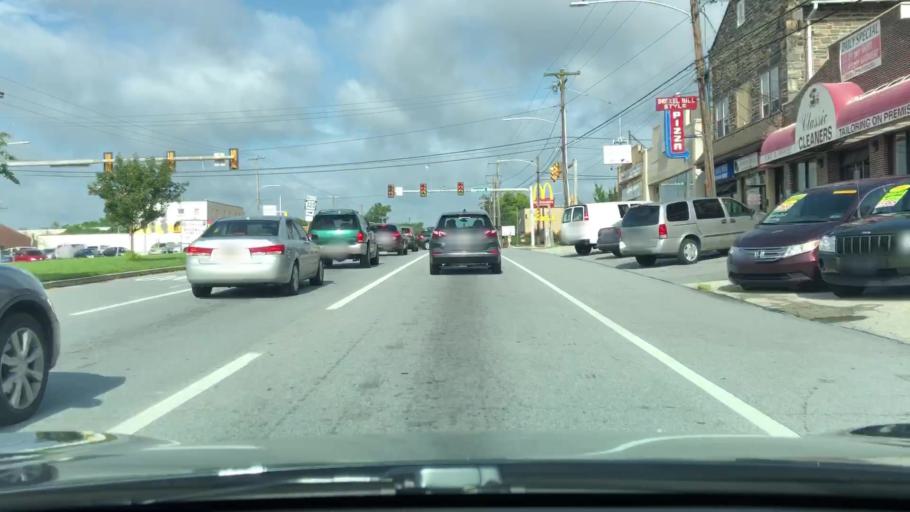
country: US
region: Pennsylvania
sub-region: Delaware County
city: Broomall
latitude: 39.9818
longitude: -75.3603
